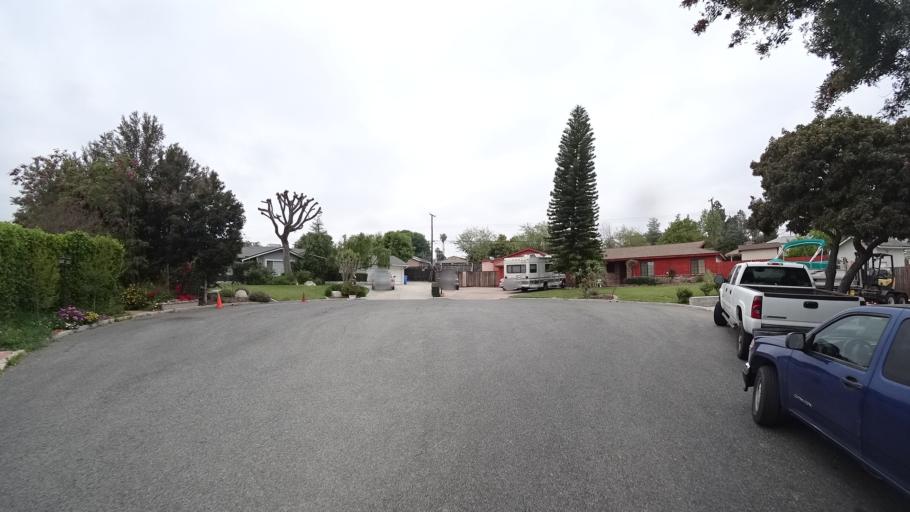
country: US
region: California
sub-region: Ventura County
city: Thousand Oaks
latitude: 34.2068
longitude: -118.8607
